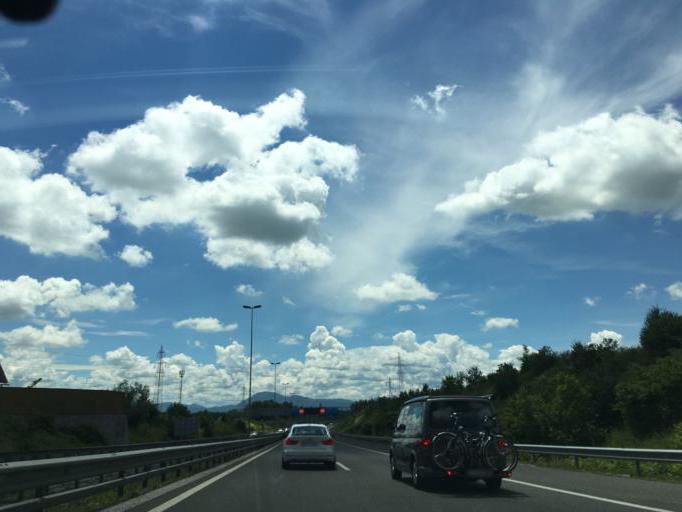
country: SI
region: Ljubljana
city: Ljubljana
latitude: 46.0827
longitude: 14.4604
